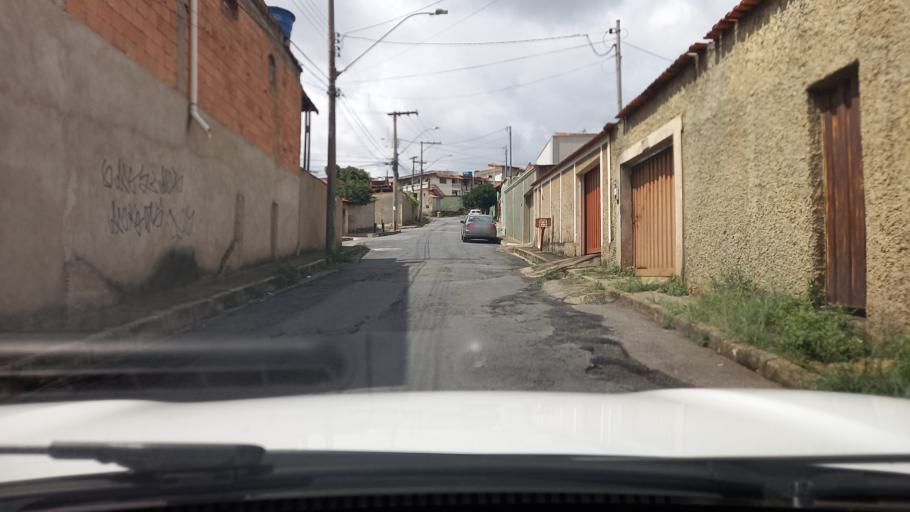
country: BR
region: Minas Gerais
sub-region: Contagem
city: Contagem
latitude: -19.9016
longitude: -44.0260
